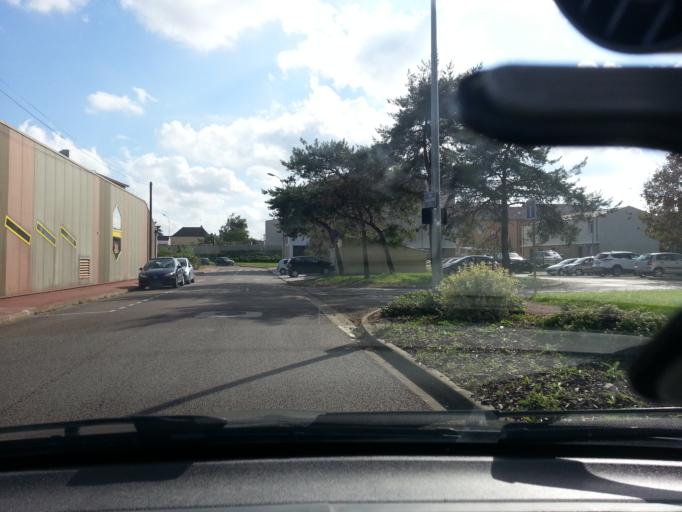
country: FR
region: Bourgogne
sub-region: Departement de Saone-et-Loire
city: Chalon-sur-Saone
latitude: 46.8011
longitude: 4.8589
